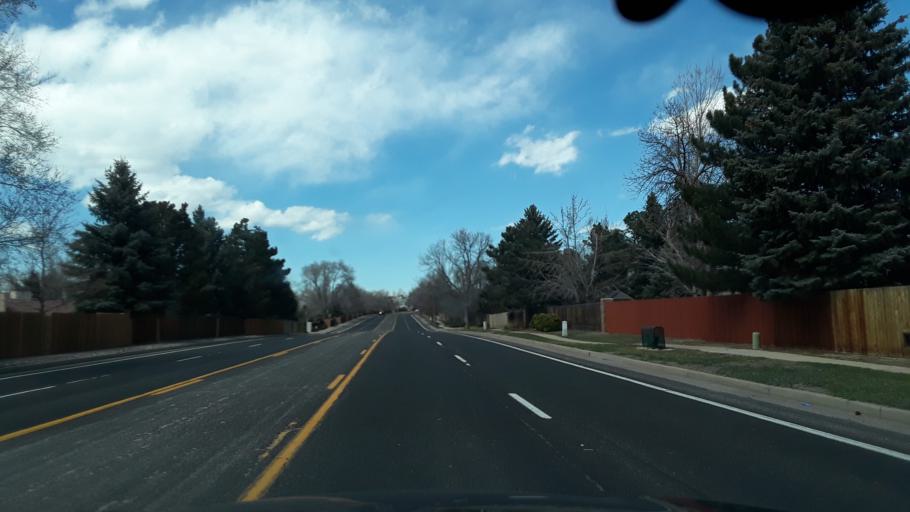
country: US
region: Colorado
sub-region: El Paso County
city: Black Forest
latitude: 38.9510
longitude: -104.7512
